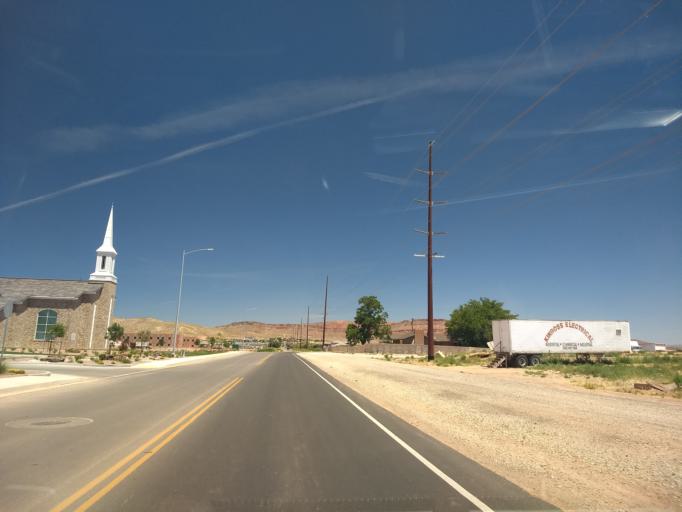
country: US
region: Utah
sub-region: Washington County
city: Washington
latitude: 37.0888
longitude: -113.5198
